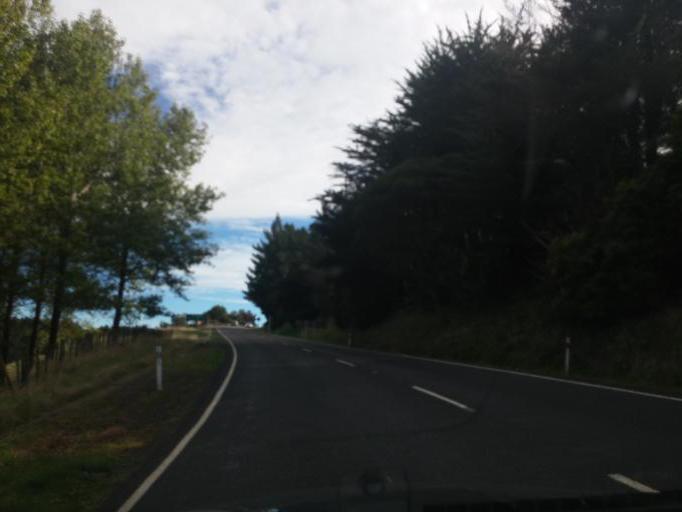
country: NZ
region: Manawatu-Wanganui
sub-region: Palmerston North City
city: Palmerston North
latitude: -40.3906
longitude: 175.6373
